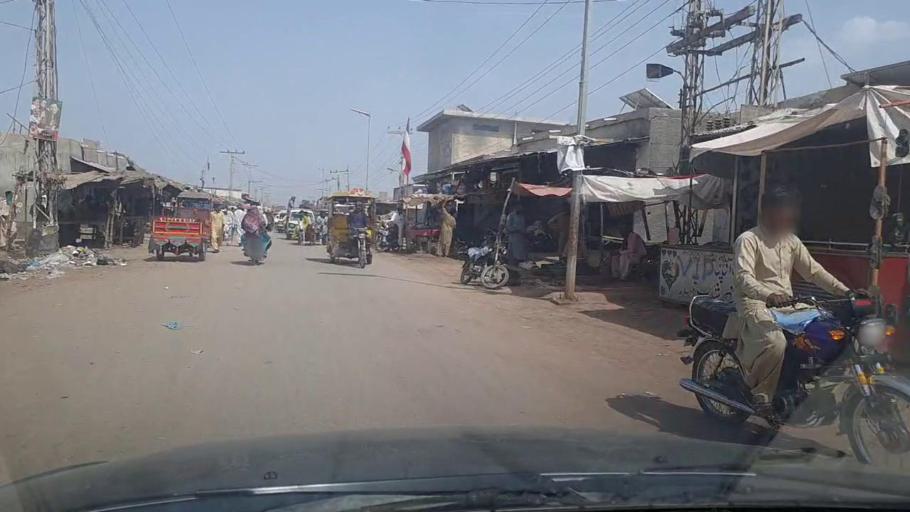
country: PK
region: Sindh
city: Talhar
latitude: 24.8844
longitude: 68.8145
